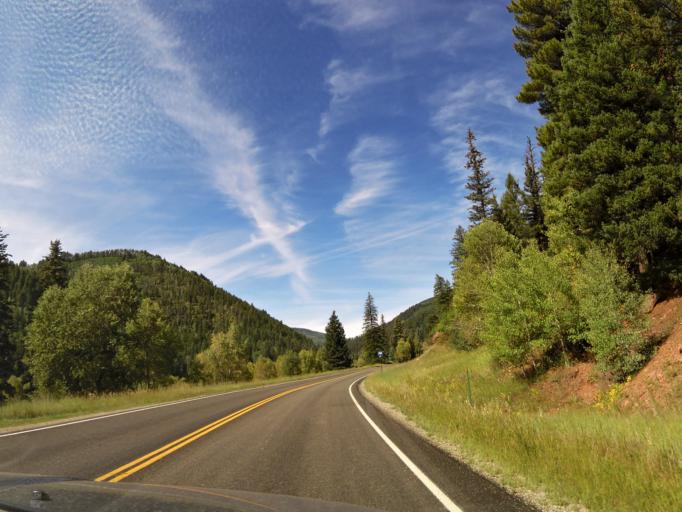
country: US
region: Colorado
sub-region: Montezuma County
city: Mancos
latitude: 37.5882
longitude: -108.1494
